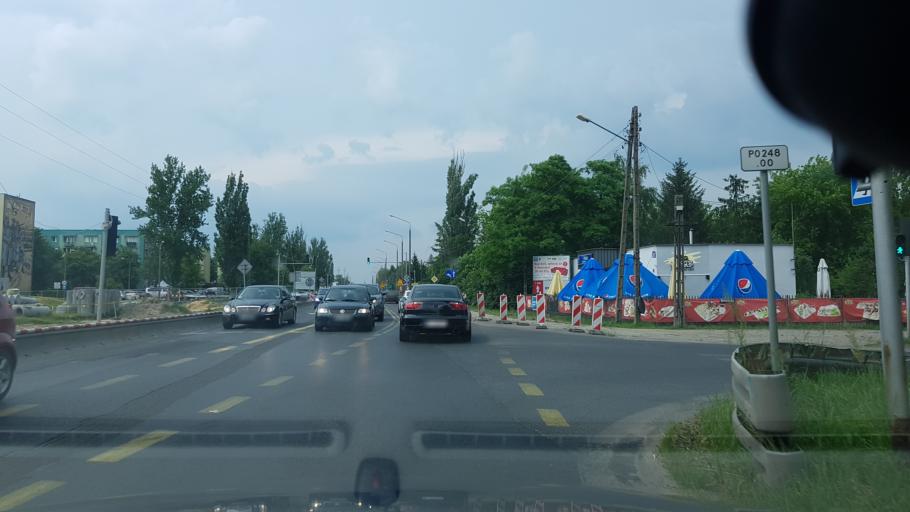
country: PL
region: Masovian Voivodeship
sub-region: Powiat legionowski
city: Michalow-Reginow
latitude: 52.4042
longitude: 20.9498
